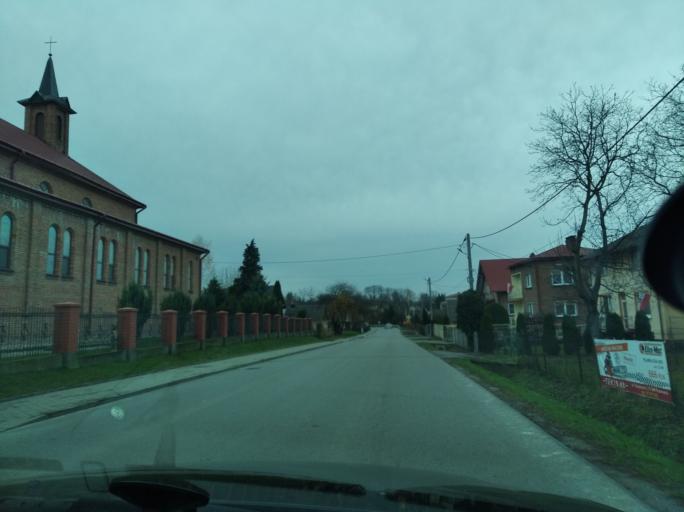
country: PL
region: Subcarpathian Voivodeship
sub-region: Powiat przeworski
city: Debow
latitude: 50.0446
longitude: 22.4392
